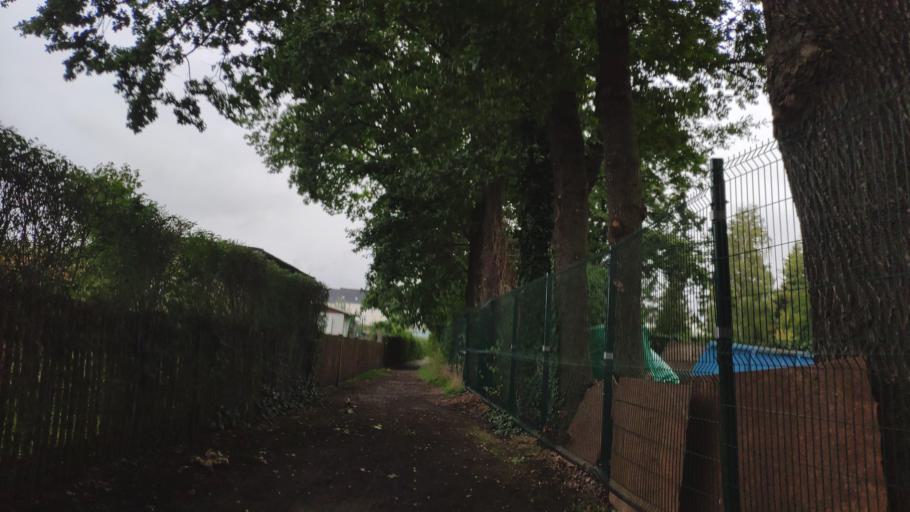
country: DE
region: Saxony
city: Chemnitz
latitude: 50.8269
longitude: 12.9529
